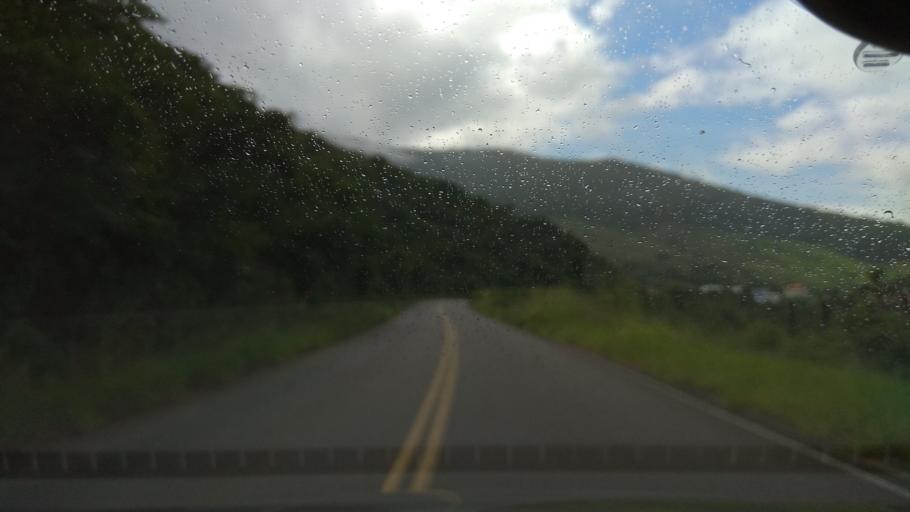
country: BR
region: Bahia
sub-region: Ubaira
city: Ubaira
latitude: -13.2509
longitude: -39.7213
